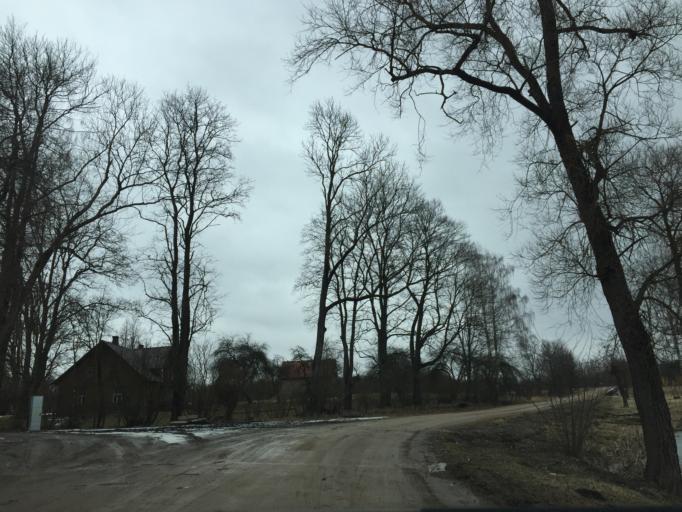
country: LV
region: Lielvarde
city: Lielvarde
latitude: 56.7566
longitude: 24.7824
